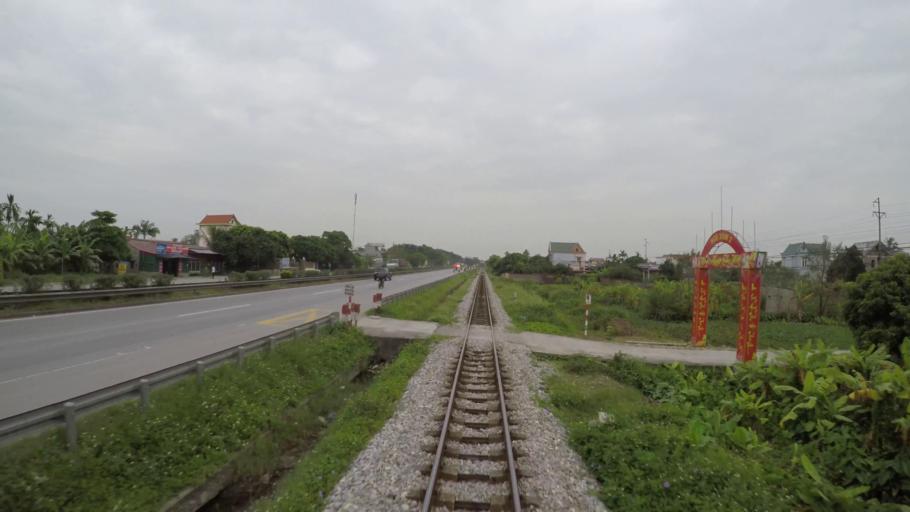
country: VN
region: Hai Duong
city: Phu Thai
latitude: 20.9688
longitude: 106.4602
